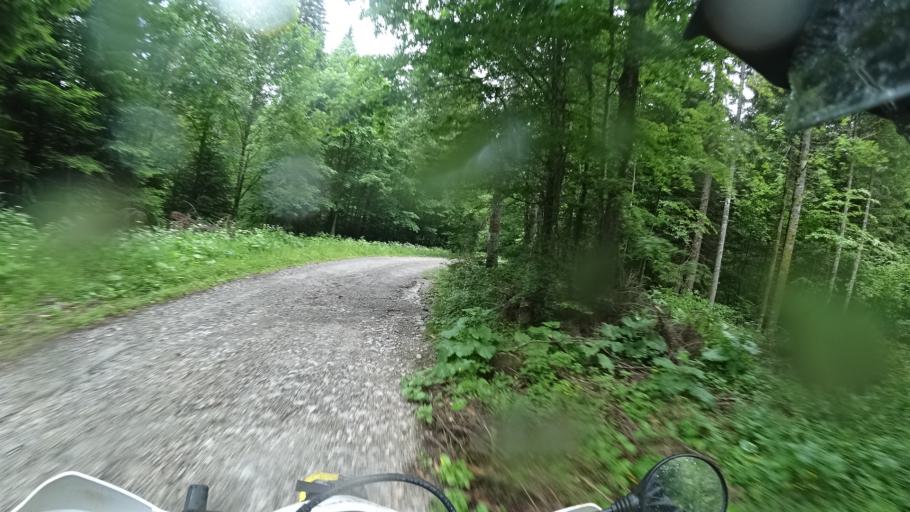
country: HR
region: Primorsko-Goranska
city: Vrbovsko
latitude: 45.3041
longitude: 14.9382
